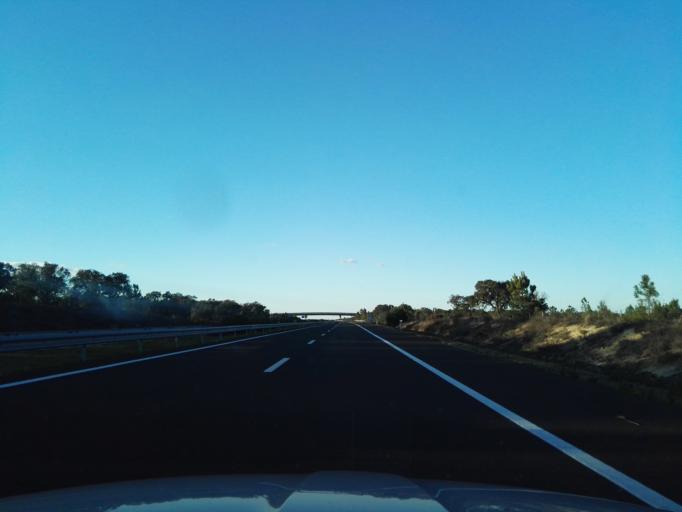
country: PT
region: Santarem
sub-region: Benavente
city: Poceirao
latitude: 38.8256
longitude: -8.7162
